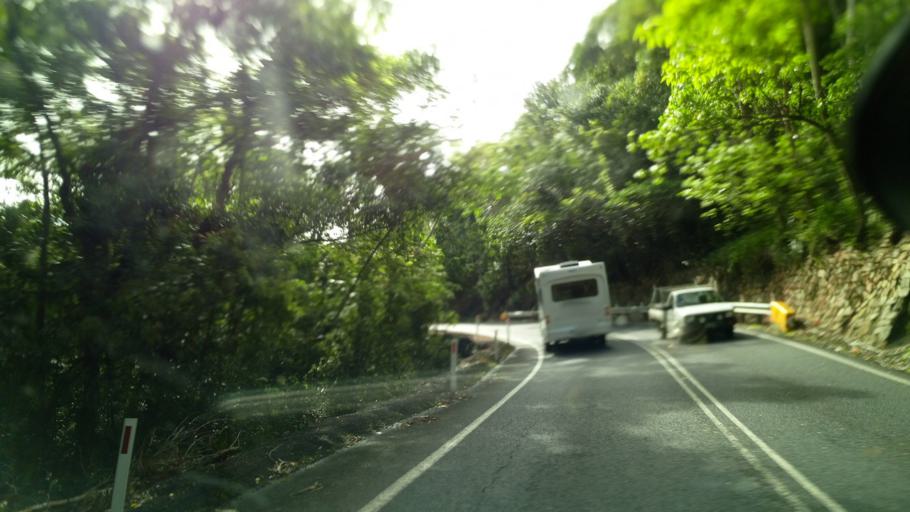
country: AU
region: Queensland
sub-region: Cairns
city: Redlynch
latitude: -16.8501
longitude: 145.6862
